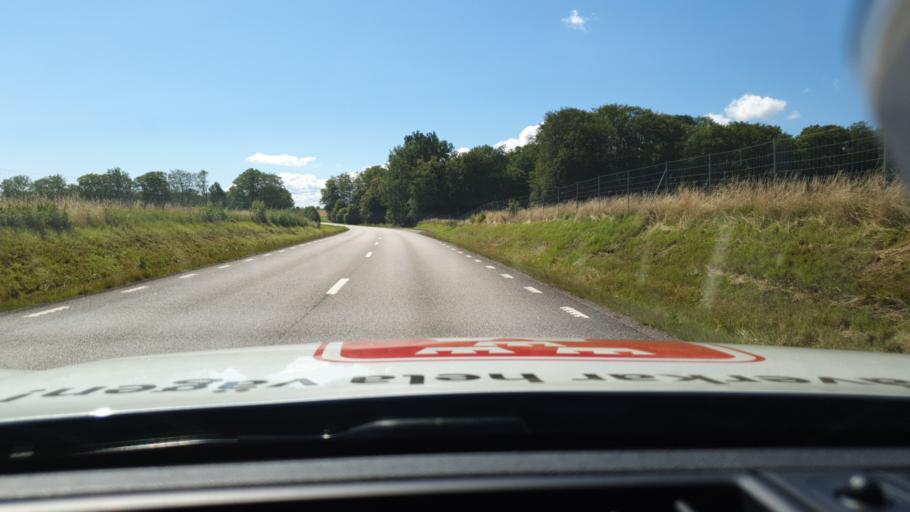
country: SE
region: Vaestra Goetaland
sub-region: Hjo Kommun
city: Hjo
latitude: 58.3435
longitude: 14.3416
